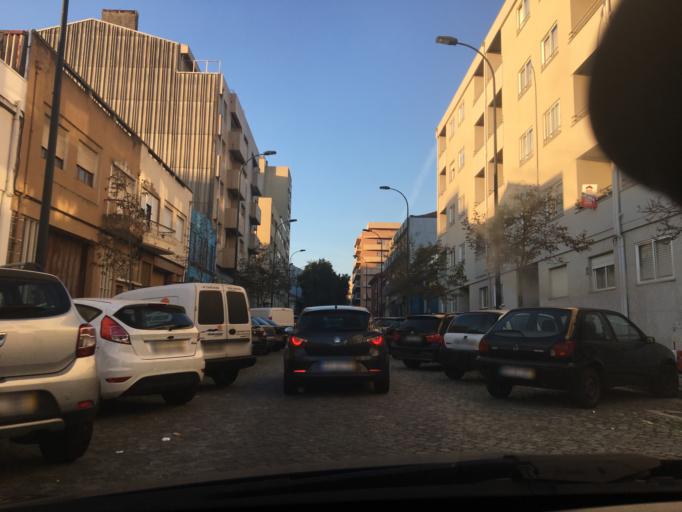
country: PT
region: Porto
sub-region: Matosinhos
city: Matosinhos
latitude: 41.1791
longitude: -8.6875
